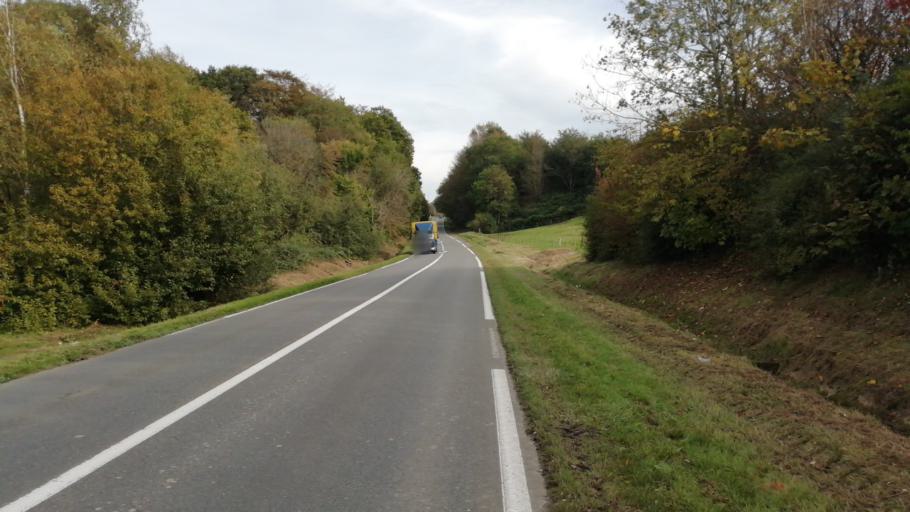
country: FR
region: Haute-Normandie
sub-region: Departement de la Seine-Maritime
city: Epouville
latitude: 49.5485
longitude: 0.2130
